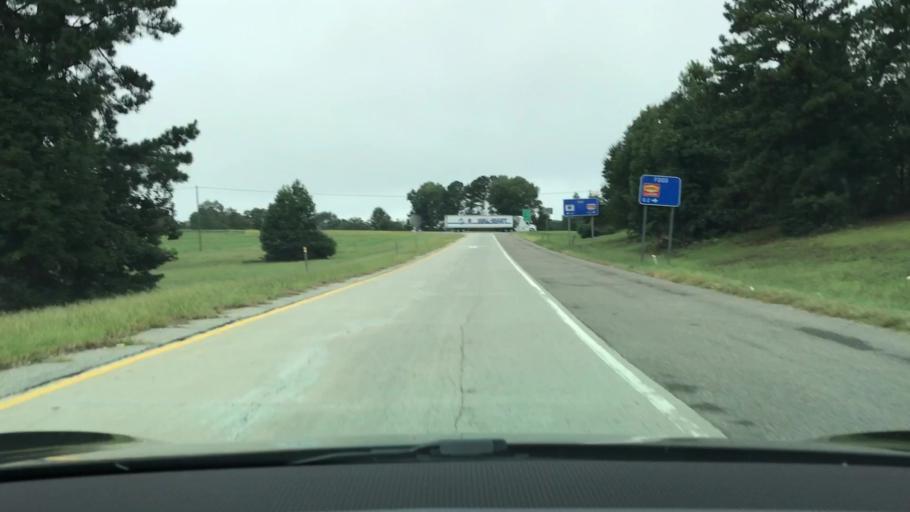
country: US
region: Georgia
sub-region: Greene County
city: Union Point
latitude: 33.5449
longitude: -83.0776
